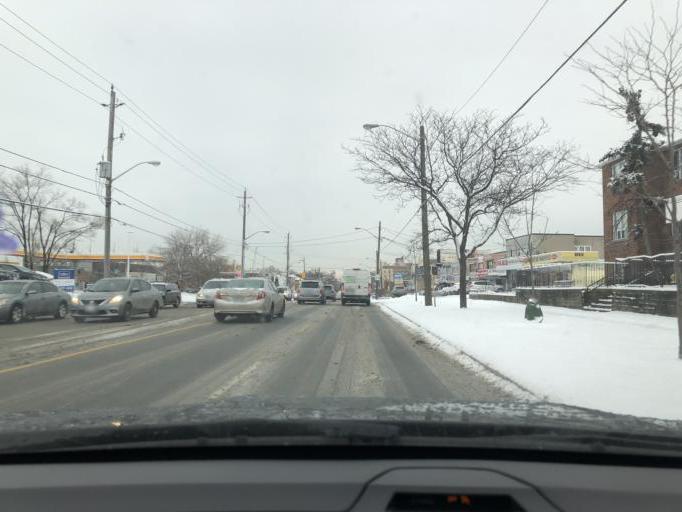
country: CA
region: Ontario
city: Toronto
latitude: 43.7042
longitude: -79.4771
